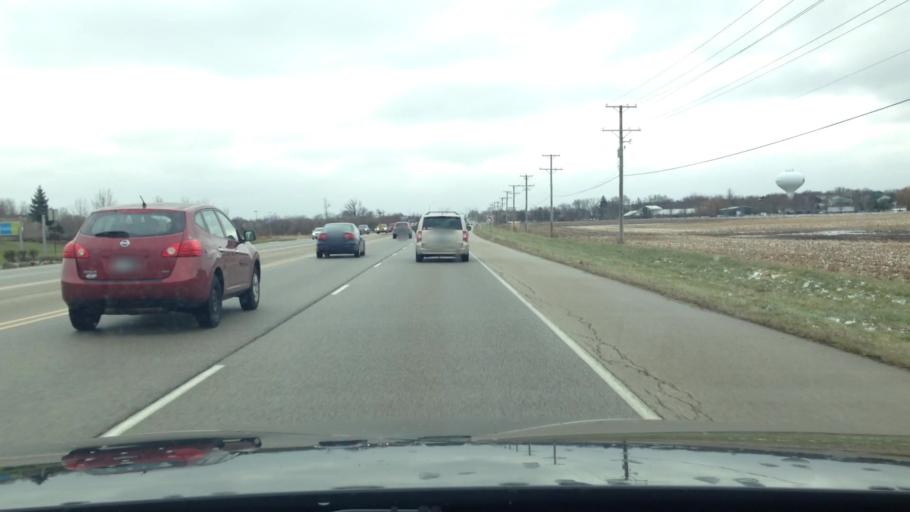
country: US
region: Illinois
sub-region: Kane County
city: Gilberts
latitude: 42.1338
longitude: -88.3357
